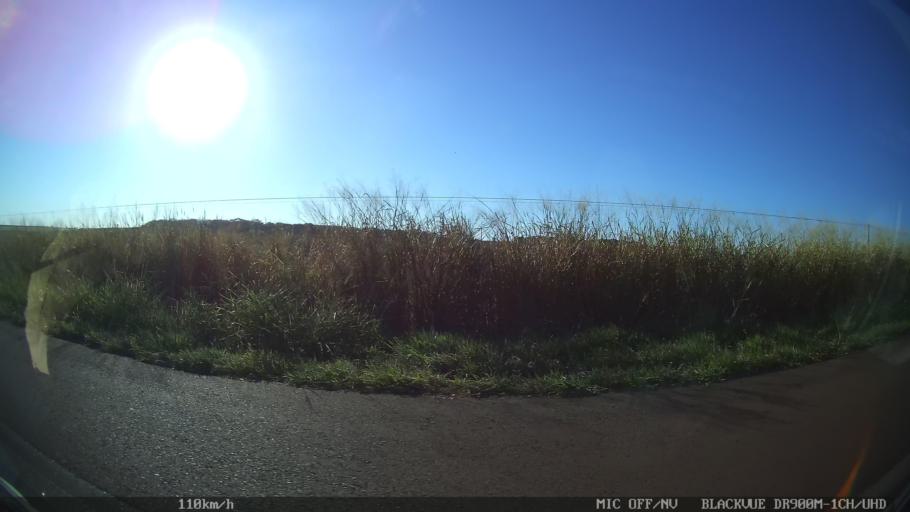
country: BR
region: Sao Paulo
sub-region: Guapiacu
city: Guapiacu
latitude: -20.7413
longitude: -49.0987
